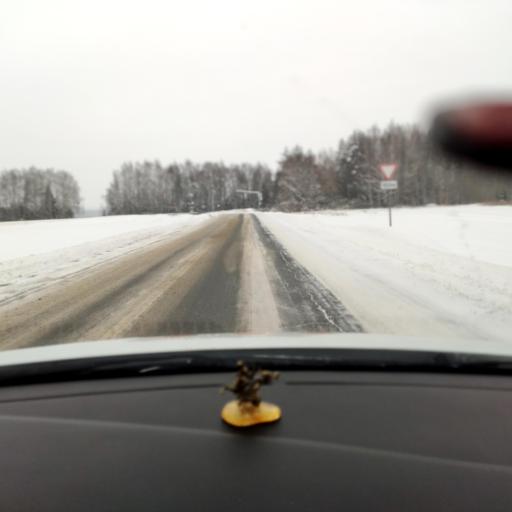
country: RU
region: Tatarstan
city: Vysokaya Gora
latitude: 56.1083
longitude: 49.1750
